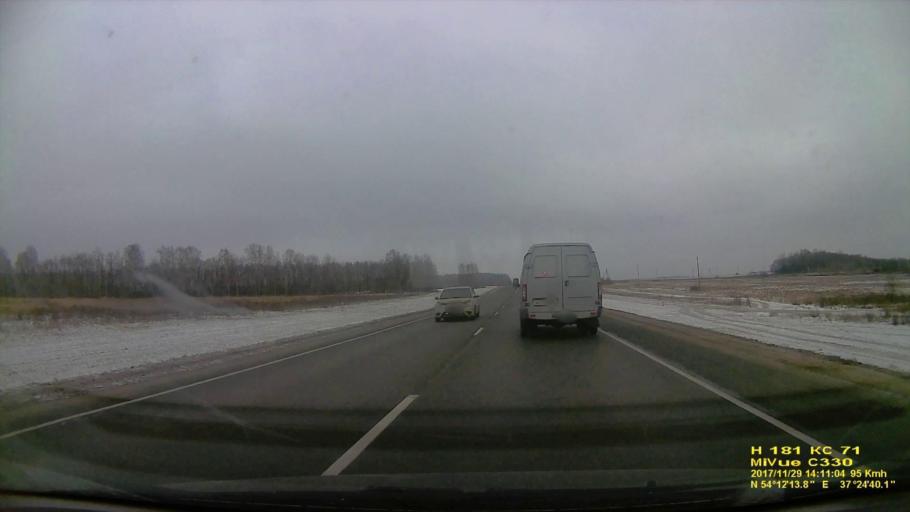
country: RU
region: Tula
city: Leninskiy
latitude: 54.2036
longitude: 37.4115
